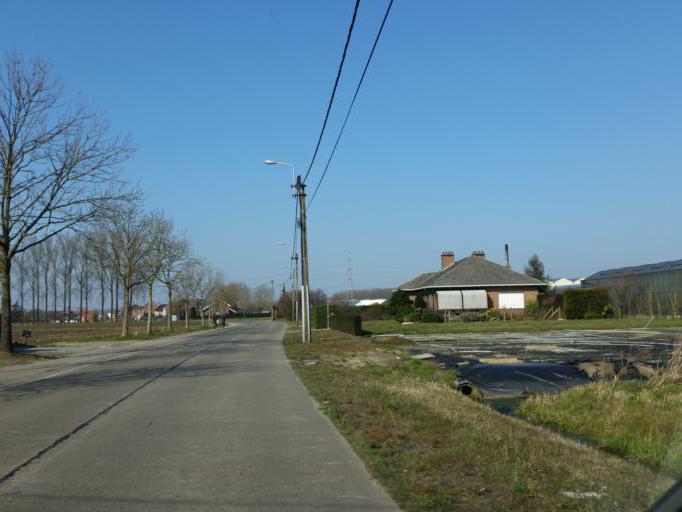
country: BE
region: Flanders
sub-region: Provincie Oost-Vlaanderen
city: Wachtebeke
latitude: 51.1308
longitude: 3.8791
